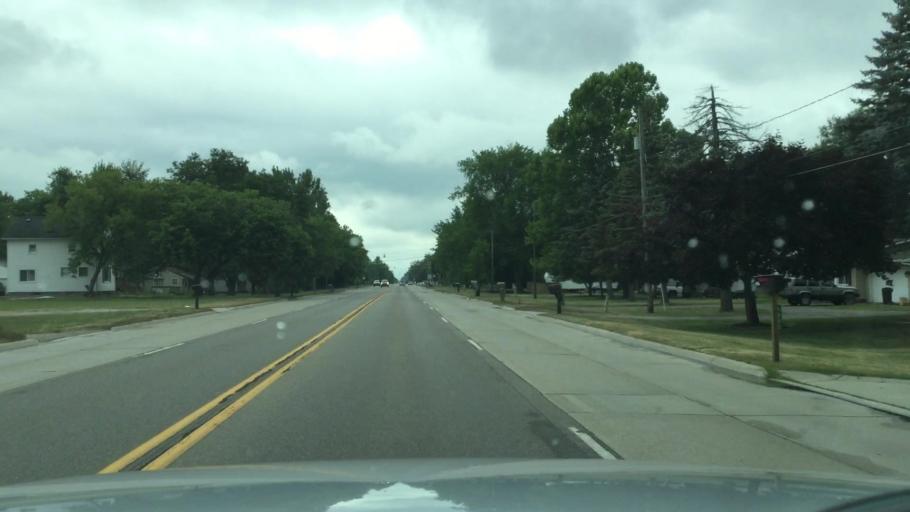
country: US
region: Michigan
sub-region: Genesee County
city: Burton
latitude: 43.0642
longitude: -83.6164
